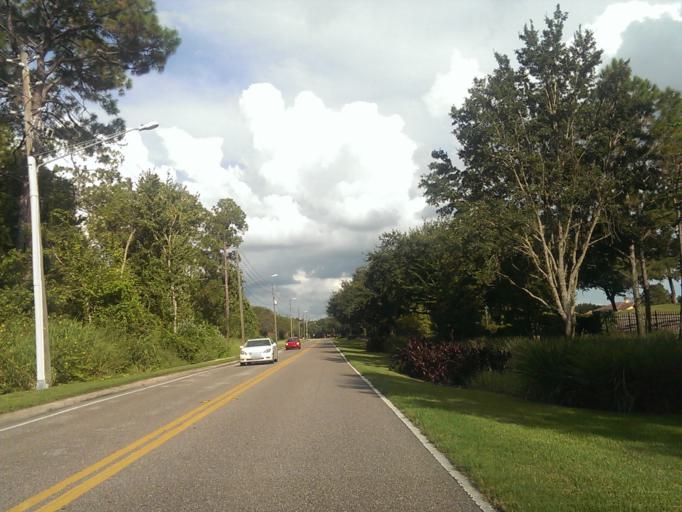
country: US
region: Florida
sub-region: Orange County
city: Bay Hill
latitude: 28.4645
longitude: -81.5455
